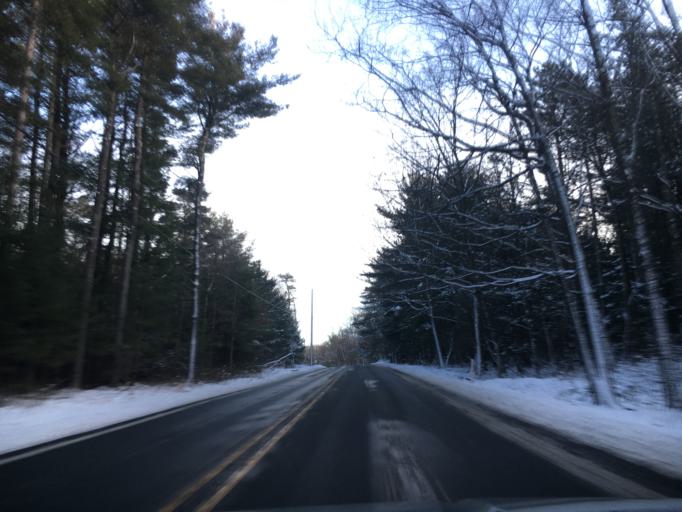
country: US
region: Pennsylvania
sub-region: Pike County
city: Hemlock Farms
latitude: 41.3199
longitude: -75.1147
